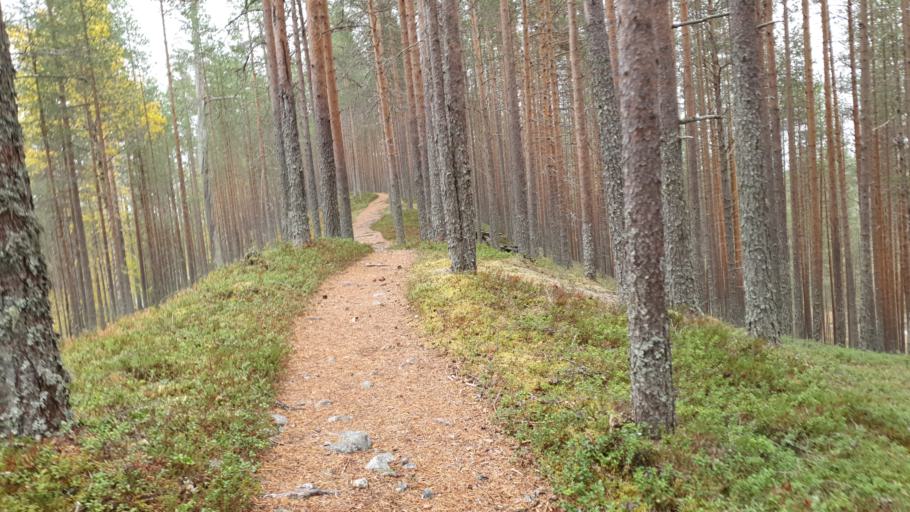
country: FI
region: Kainuu
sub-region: Kehys-Kainuu
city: Kuhmo
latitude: 64.2928
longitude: 29.3624
